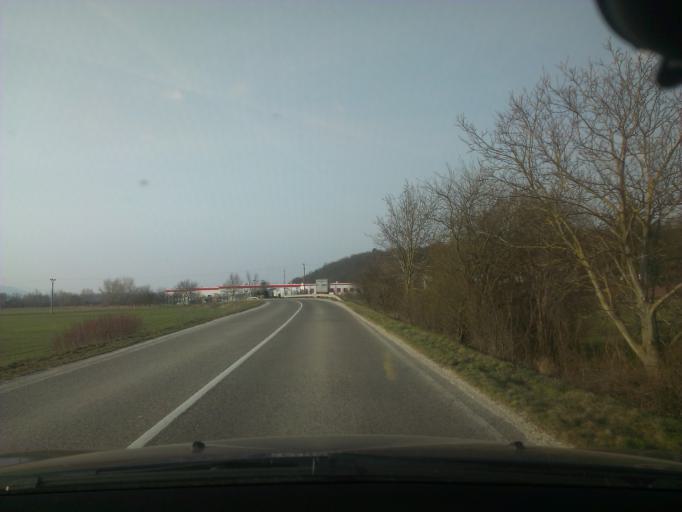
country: SK
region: Trnavsky
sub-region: Okres Trnava
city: Piestany
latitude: 48.6637
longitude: 17.8770
